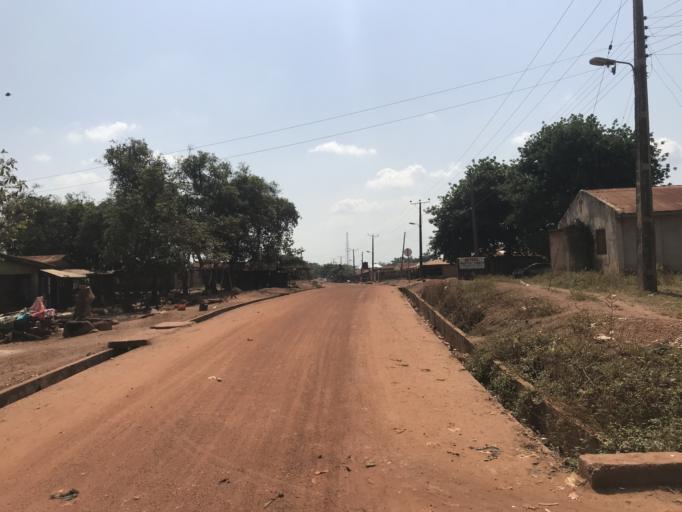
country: NG
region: Osun
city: Ifon
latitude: 7.8658
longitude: 4.4768
